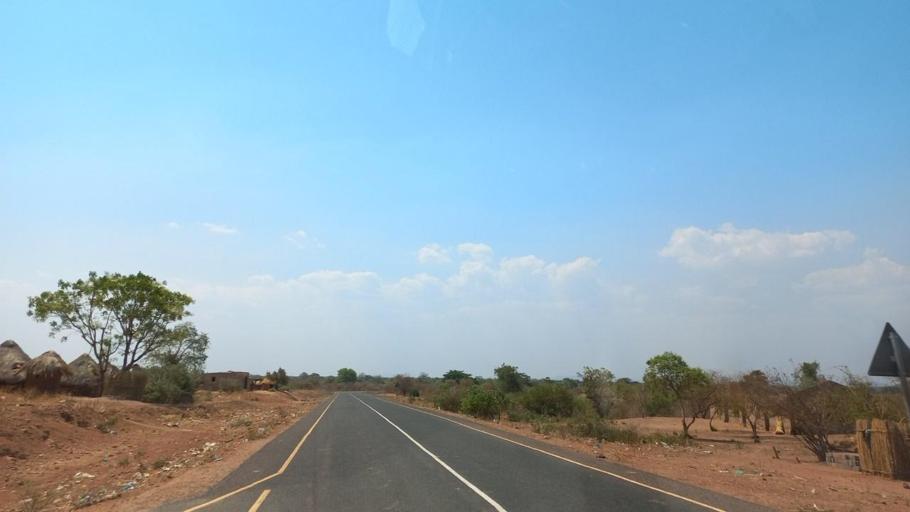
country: ZM
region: Lusaka
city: Luangwa
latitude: -15.5542
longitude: 30.3528
